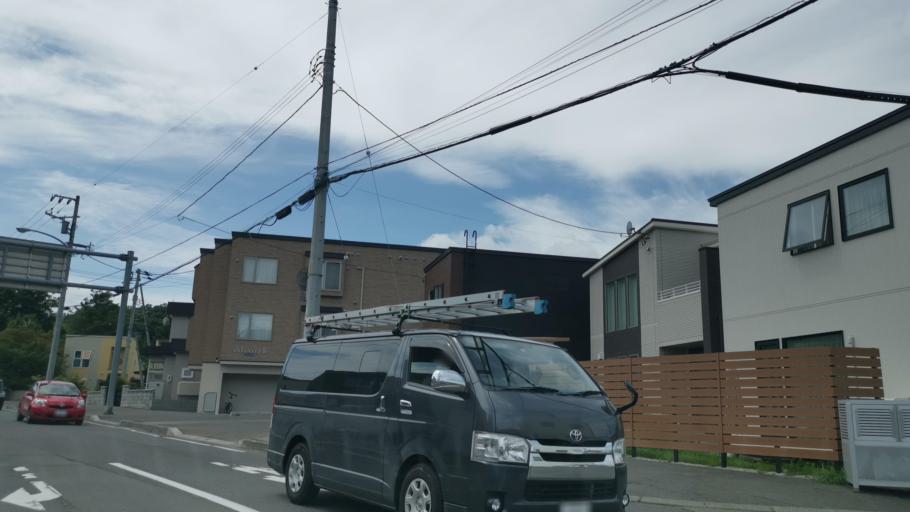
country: JP
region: Hokkaido
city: Sapporo
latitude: 42.9830
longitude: 141.3351
